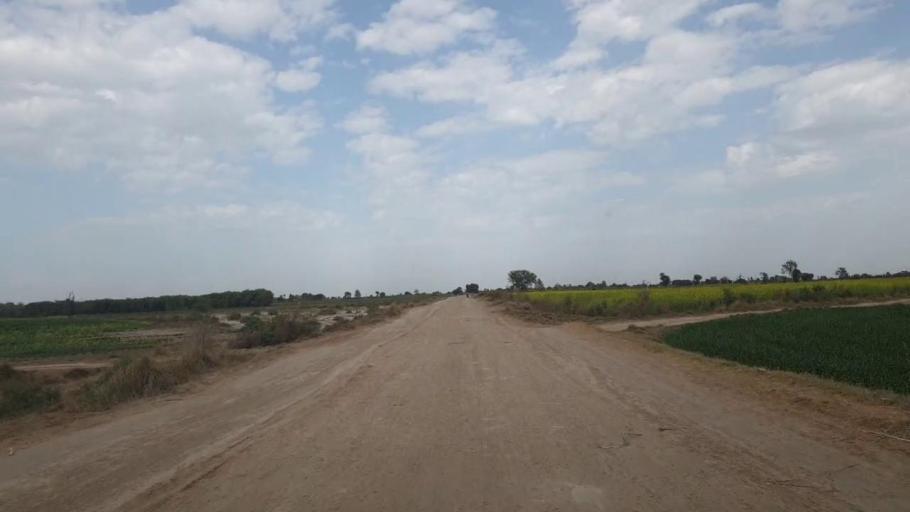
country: PK
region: Sindh
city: Hala
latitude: 25.9594
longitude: 68.4663
